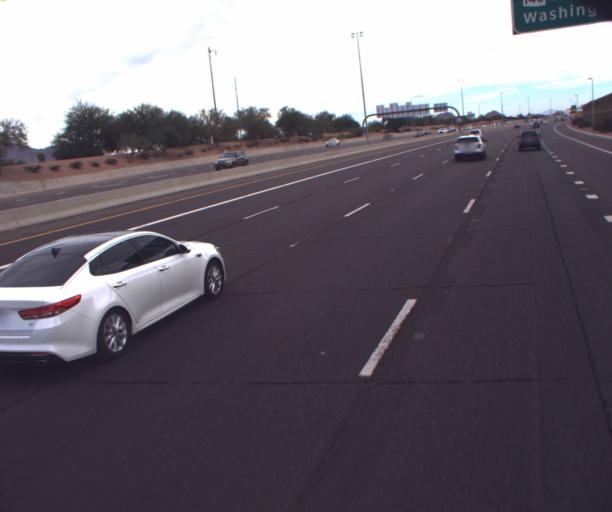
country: US
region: Arizona
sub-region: Maricopa County
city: Phoenix
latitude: 33.4619
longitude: -112.0223
